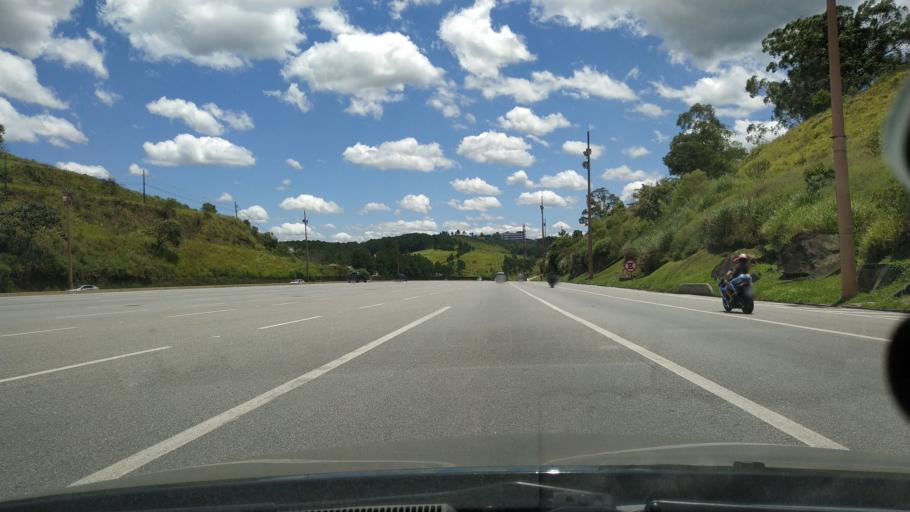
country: BR
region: Sao Paulo
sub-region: Itapevi
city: Itapevi
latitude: -23.5178
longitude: -46.9417
